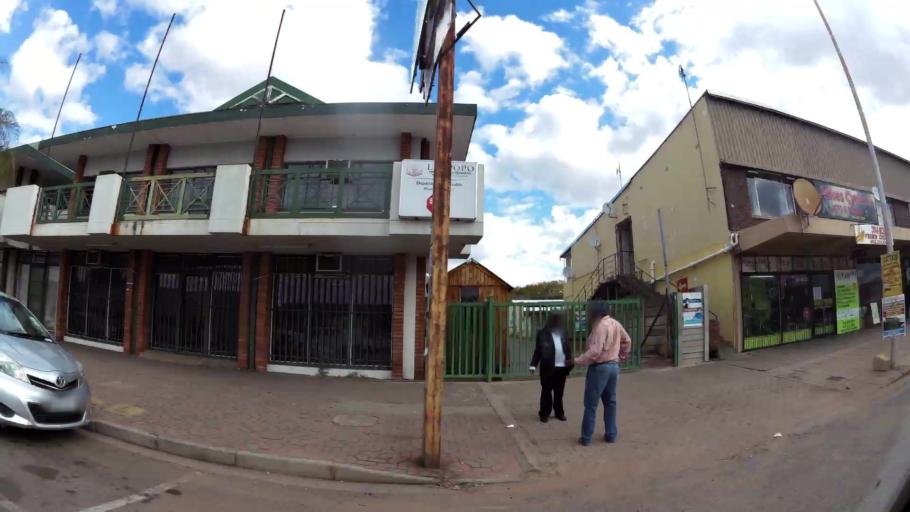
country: ZA
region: Limpopo
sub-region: Waterberg District Municipality
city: Modimolle
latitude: -24.7009
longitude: 28.4065
